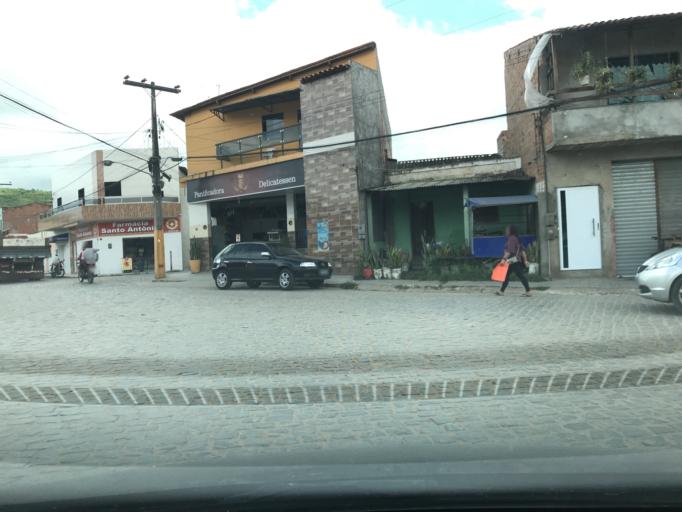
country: BR
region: Pernambuco
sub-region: Bezerros
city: Bezerros
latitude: -8.2311
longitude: -35.7588
